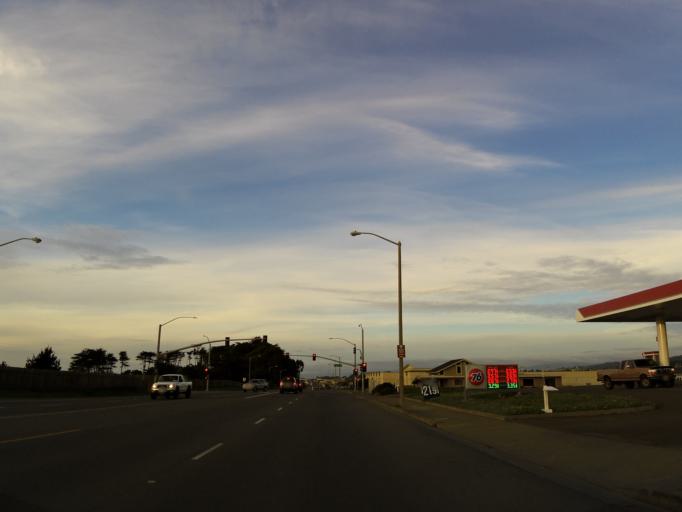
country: US
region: California
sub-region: Mendocino County
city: Fort Bragg
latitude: 39.4319
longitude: -123.8062
